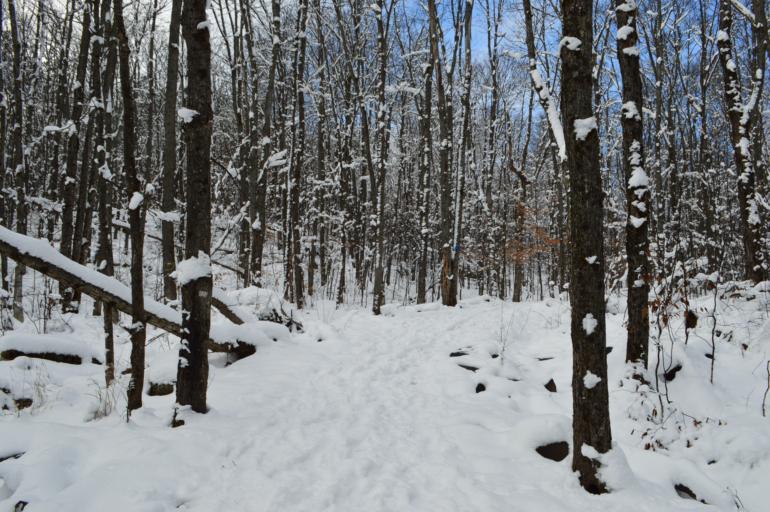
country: CA
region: Ontario
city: Bancroft
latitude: 45.5831
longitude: -78.4095
